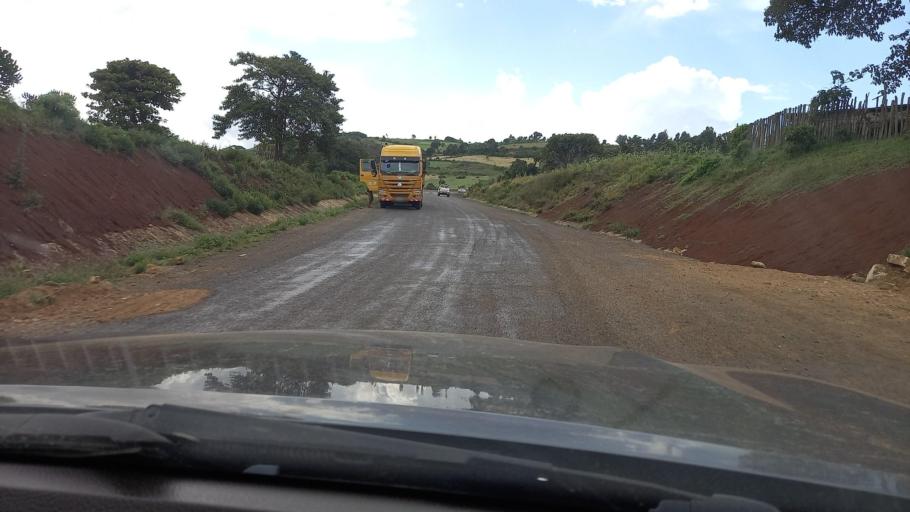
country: ET
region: Southern Nations, Nationalities, and People's Region
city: Mizan Teferi
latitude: 6.2148
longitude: 35.6391
